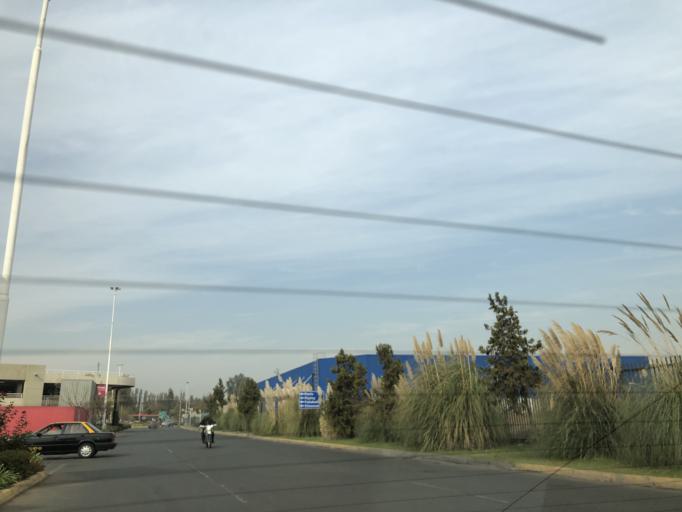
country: CL
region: Santiago Metropolitan
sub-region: Provincia de Cordillera
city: Puente Alto
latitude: -33.5701
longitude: -70.5591
